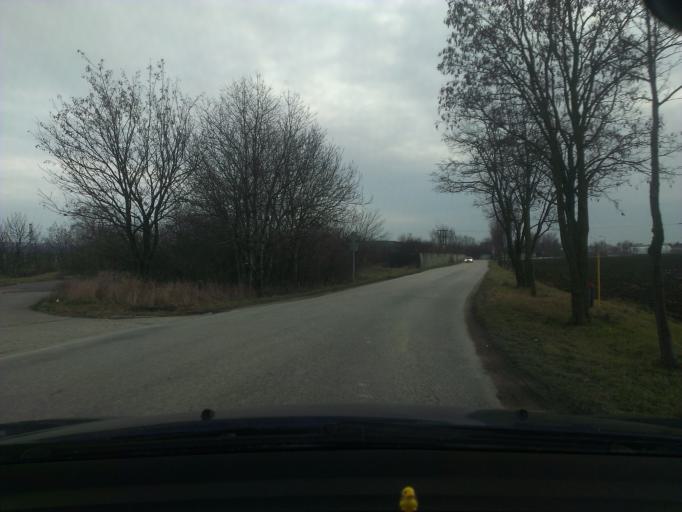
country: SK
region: Trnavsky
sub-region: Okres Trnava
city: Piestany
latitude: 48.6050
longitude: 17.8183
